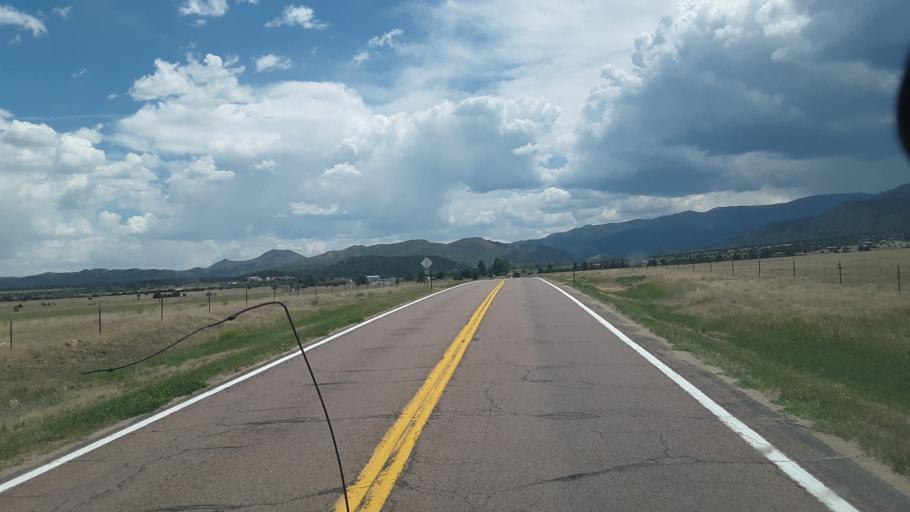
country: US
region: Colorado
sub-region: Fremont County
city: Florence
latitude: 38.2540
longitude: -105.0902
